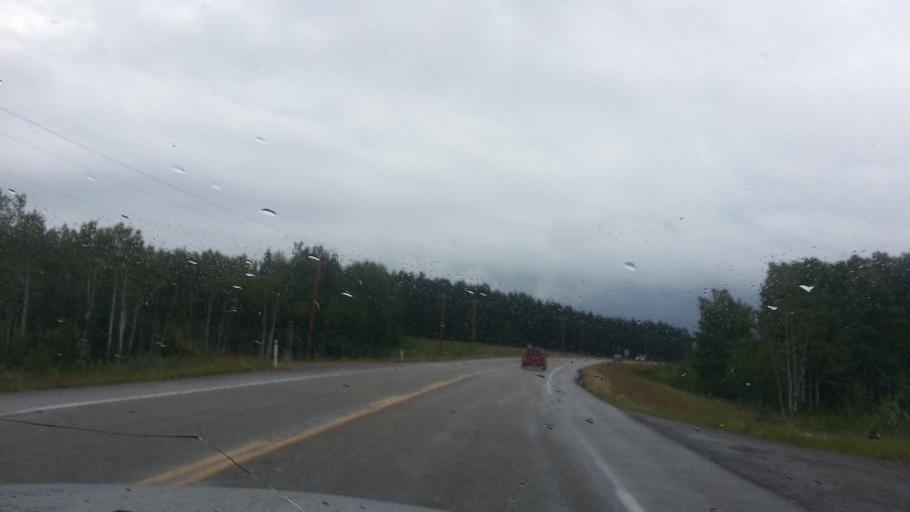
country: CA
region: Alberta
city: Cochrane
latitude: 50.9204
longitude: -114.6048
